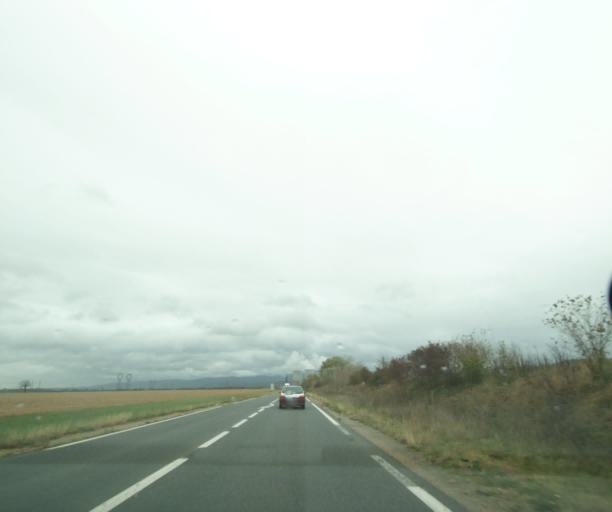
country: FR
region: Rhone-Alpes
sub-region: Departement de l'Ain
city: Loyettes
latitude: 45.7904
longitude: 5.2402
